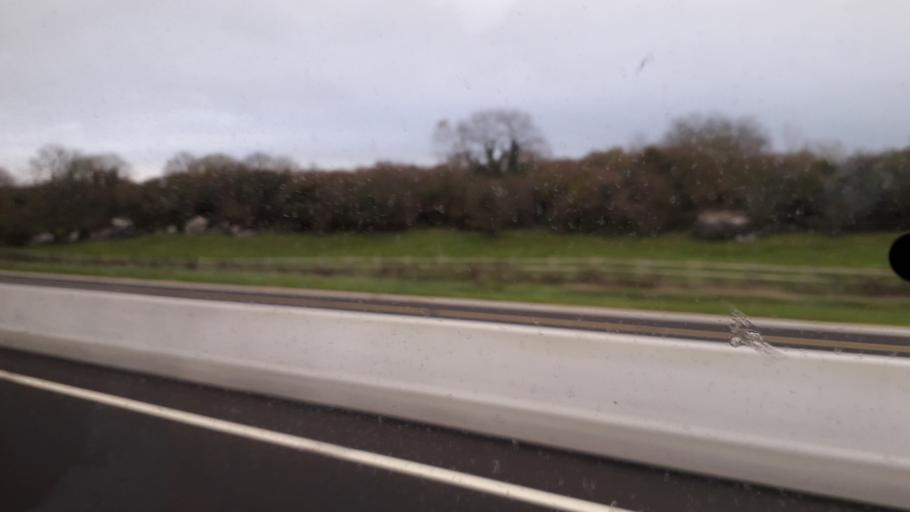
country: IE
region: Connaught
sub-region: County Galway
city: Athenry
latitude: 53.2671
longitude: -8.8122
